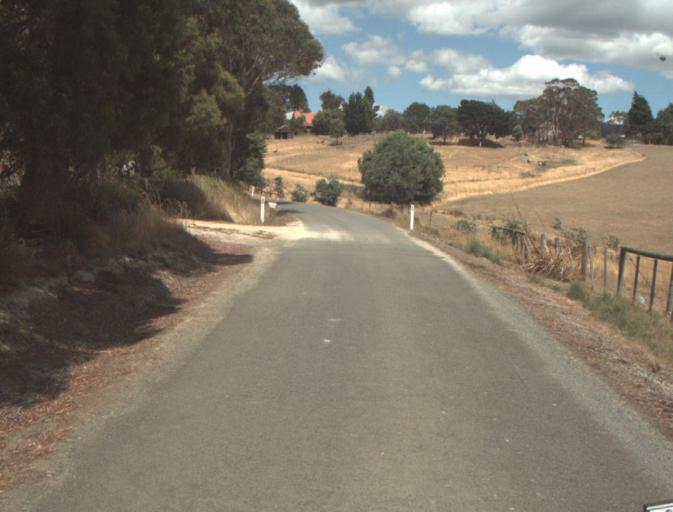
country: AU
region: Tasmania
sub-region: Launceston
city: Mayfield
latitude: -41.2146
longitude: 147.1409
